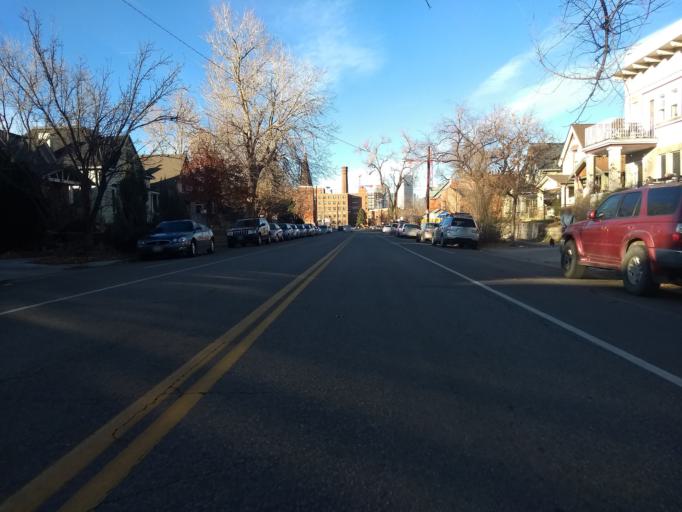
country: US
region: Colorado
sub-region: Denver County
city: Denver
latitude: 39.7229
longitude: -104.9908
